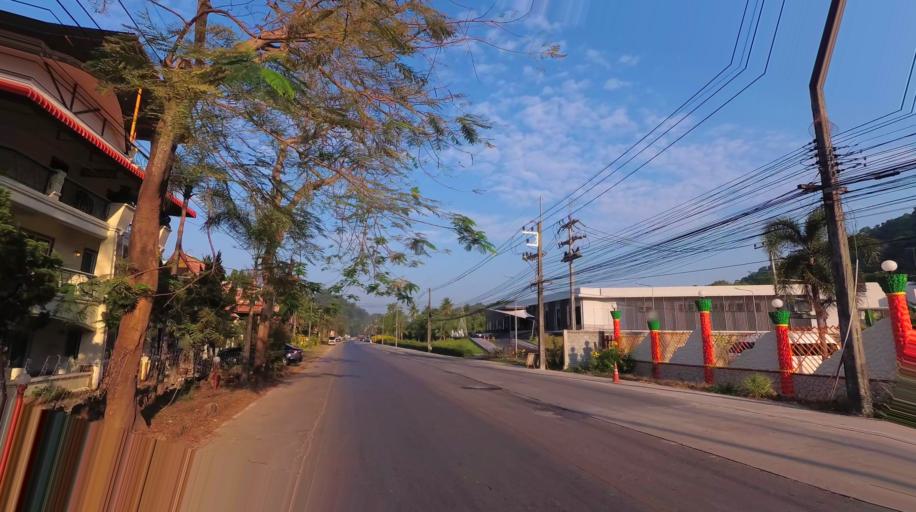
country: TH
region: Trat
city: Ko Chang Tai
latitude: 12.0663
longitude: 102.2846
